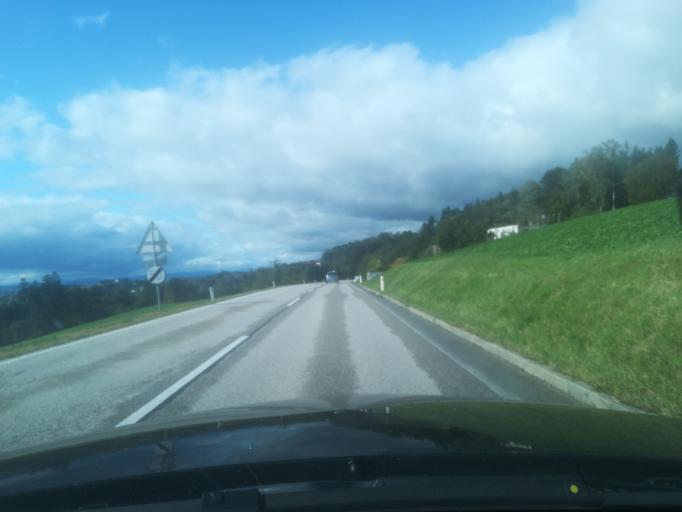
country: AT
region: Upper Austria
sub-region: Politischer Bezirk Urfahr-Umgebung
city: Eidenberg
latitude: 48.3670
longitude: 14.2280
